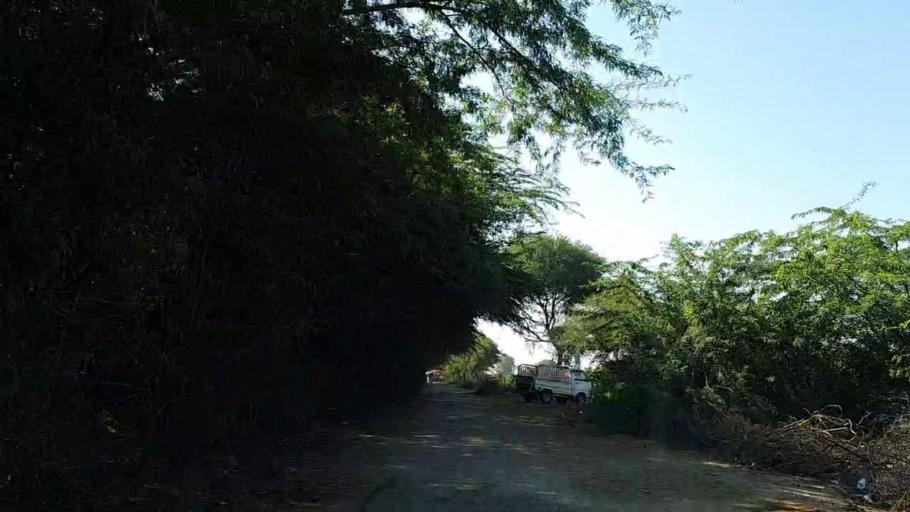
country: PK
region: Sindh
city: Chuhar Jamali
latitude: 24.5725
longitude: 68.0439
